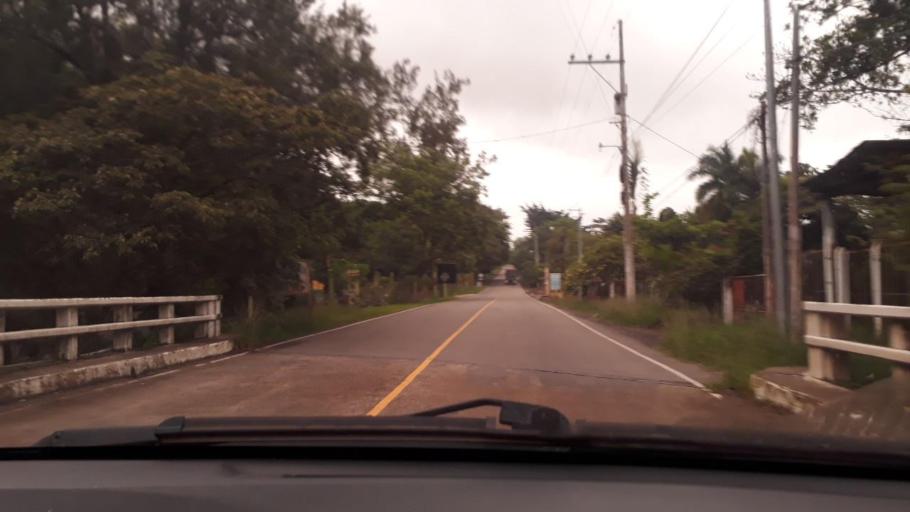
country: GT
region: Chiquimula
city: Esquipulas
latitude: 14.5626
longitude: -89.3100
